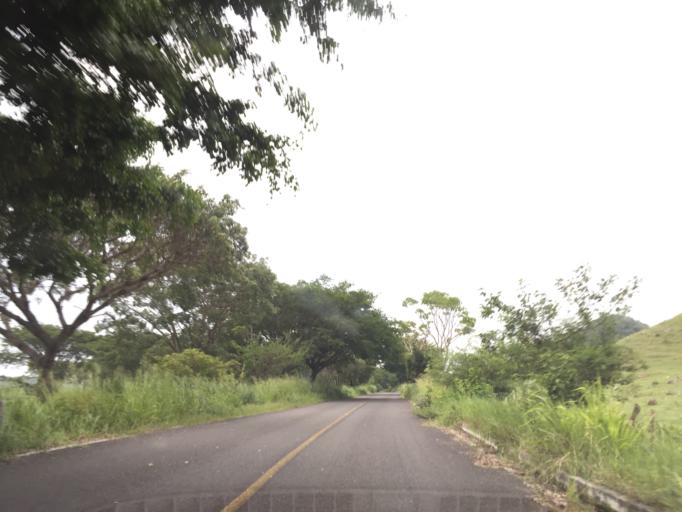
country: MX
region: Colima
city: Comala
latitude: 19.3961
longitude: -103.8035
